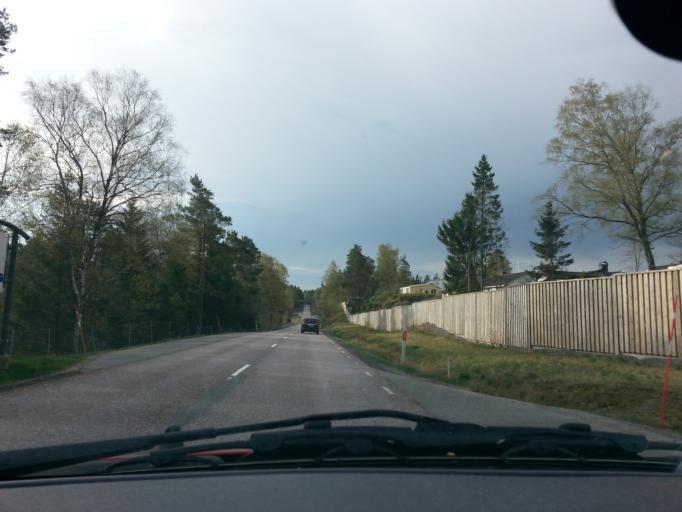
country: SE
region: Vaestra Goetaland
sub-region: Partille Kommun
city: Furulund
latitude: 57.7020
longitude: 12.1525
